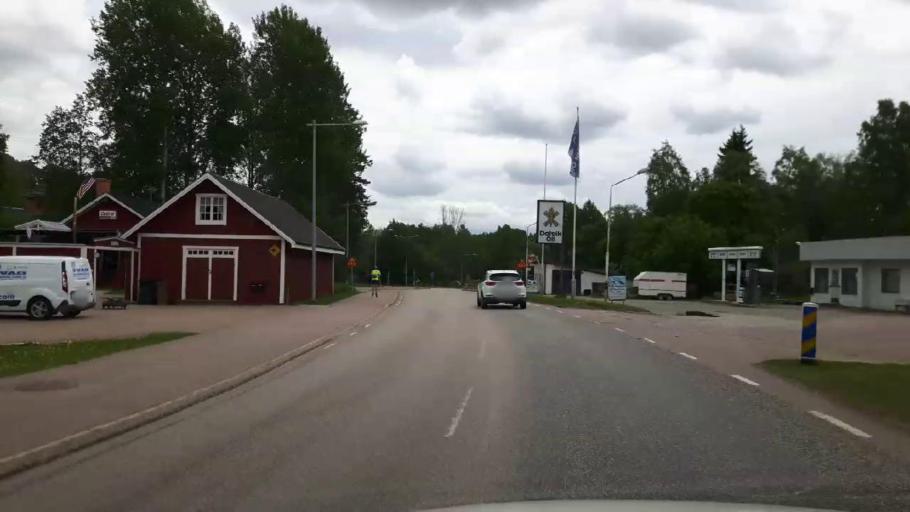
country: SE
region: Vaestmanland
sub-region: Norbergs Kommun
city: Norberg
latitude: 60.0923
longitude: 15.9353
